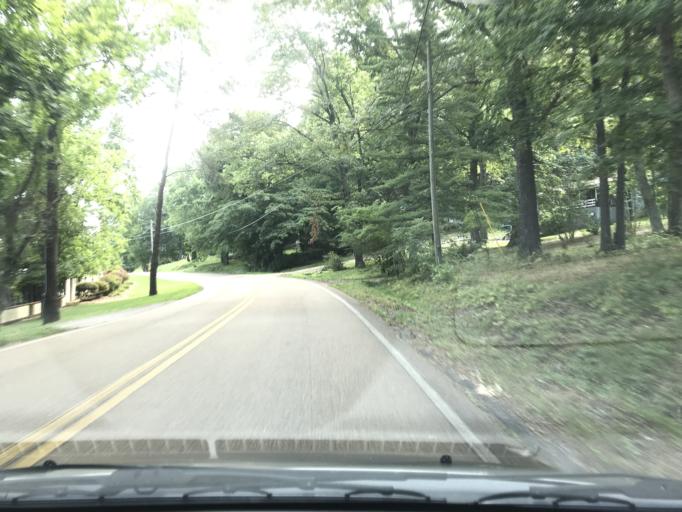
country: US
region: Tennessee
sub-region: Hamilton County
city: Lakesite
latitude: 35.2046
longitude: -85.0971
